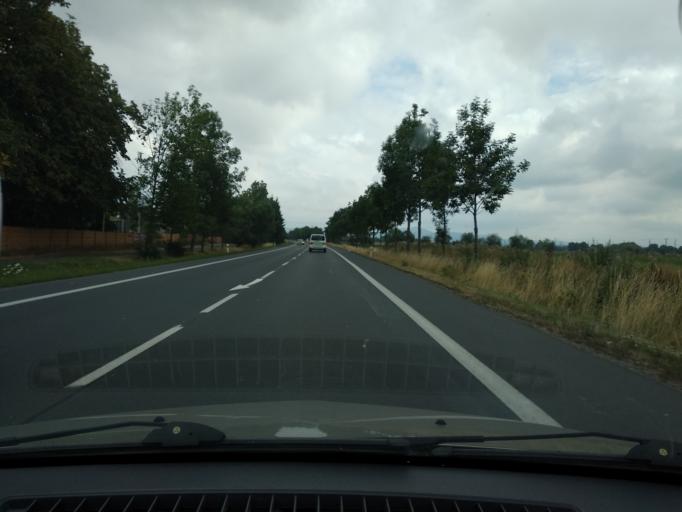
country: CZ
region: Olomoucky
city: Zabreh
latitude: 49.8793
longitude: 16.8931
